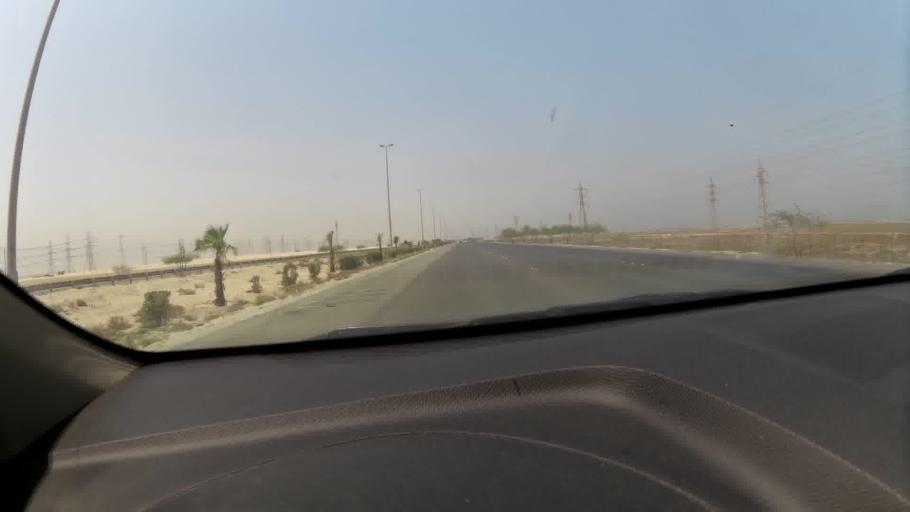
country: KW
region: Al Ahmadi
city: Al Fahahil
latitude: 28.8339
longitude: 48.2533
